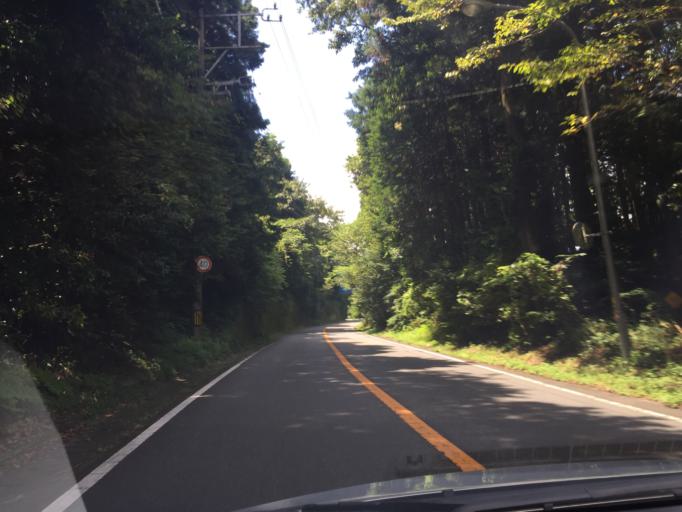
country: JP
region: Shizuoka
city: Kanaya
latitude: 34.8189
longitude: 138.1200
